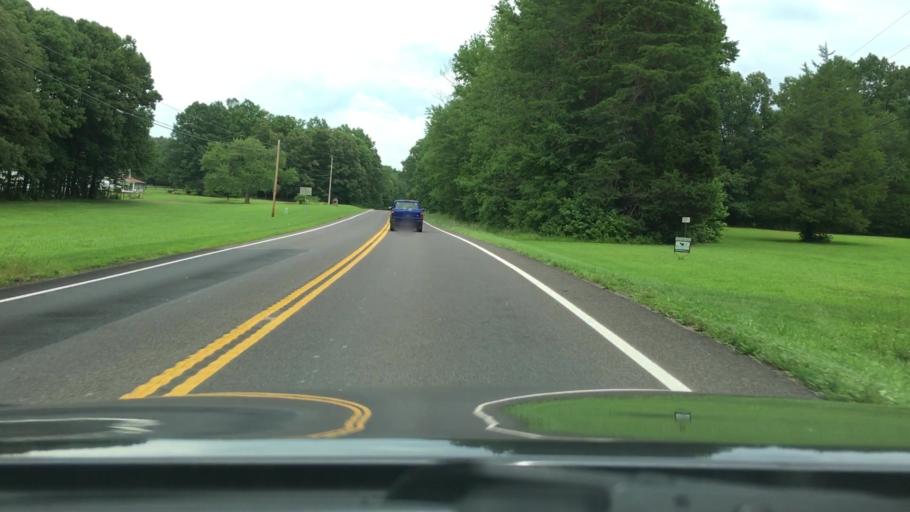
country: US
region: Virginia
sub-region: Orange County
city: Orange
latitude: 38.2590
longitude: -77.9948
